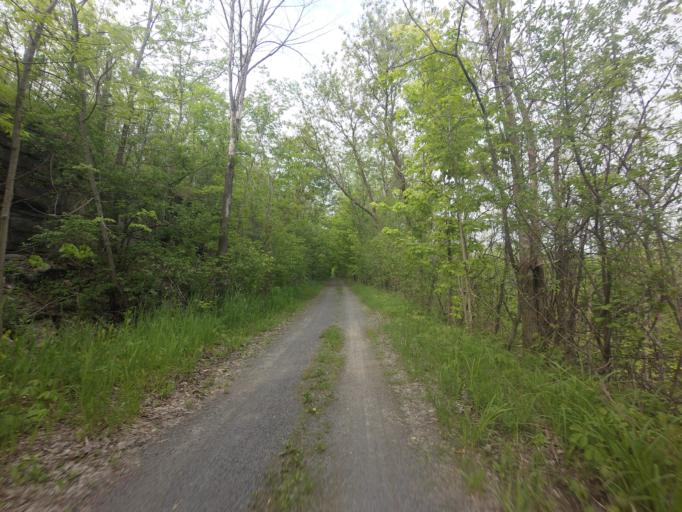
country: CA
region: Ontario
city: Kingston
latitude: 44.4099
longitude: -76.6291
